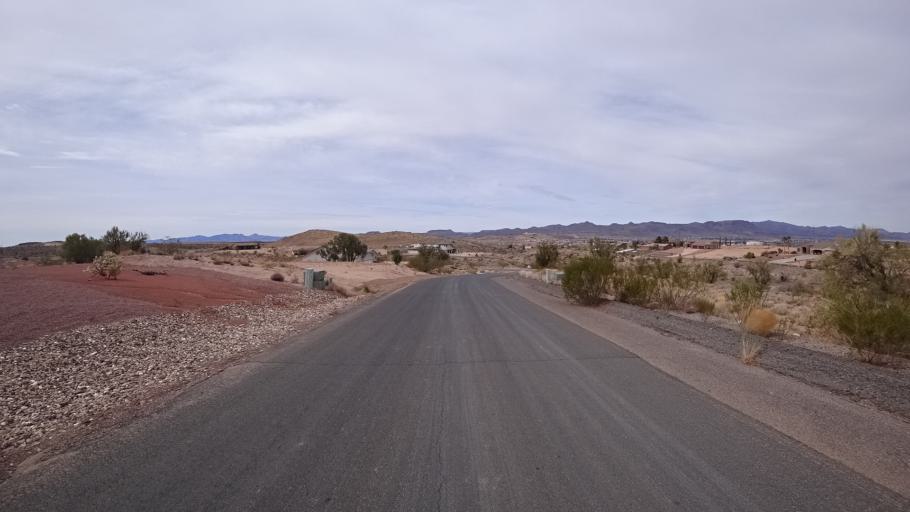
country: US
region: Arizona
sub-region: Mohave County
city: Kingman
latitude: 35.1786
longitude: -113.9991
